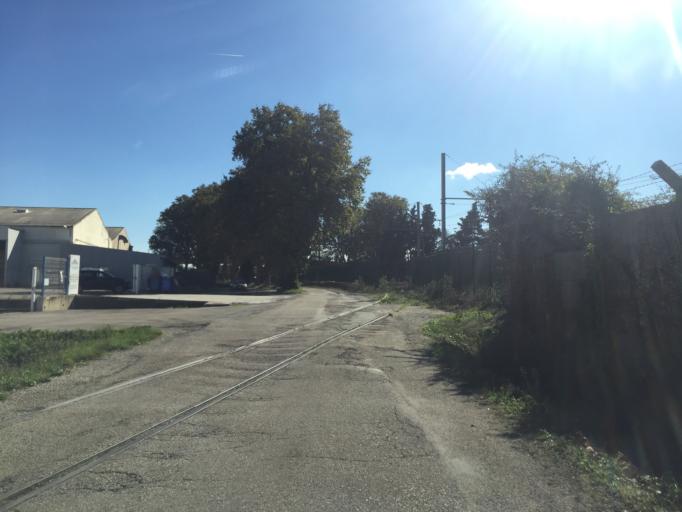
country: FR
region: Provence-Alpes-Cote d'Azur
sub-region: Departement du Vaucluse
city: Montfavet
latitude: 43.9343
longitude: 4.8449
